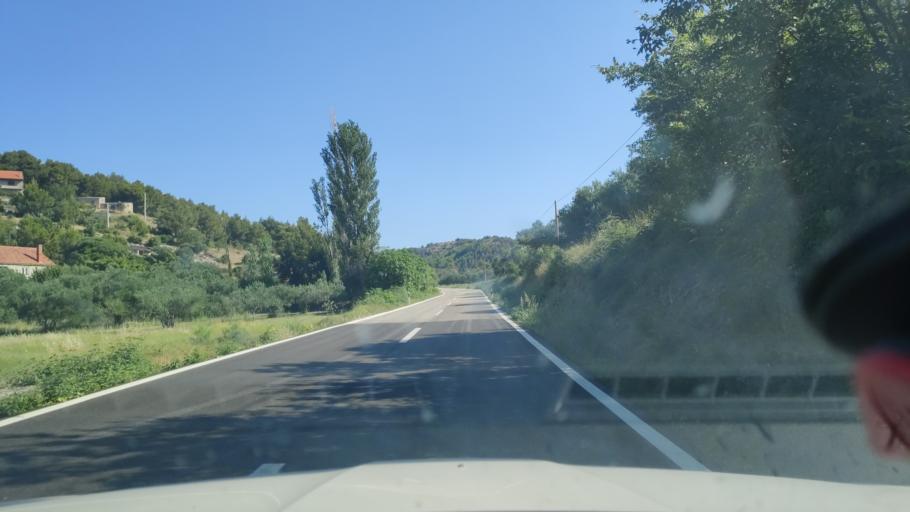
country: HR
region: Sibensko-Kniniska
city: Zaton
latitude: 43.8505
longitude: 15.8972
